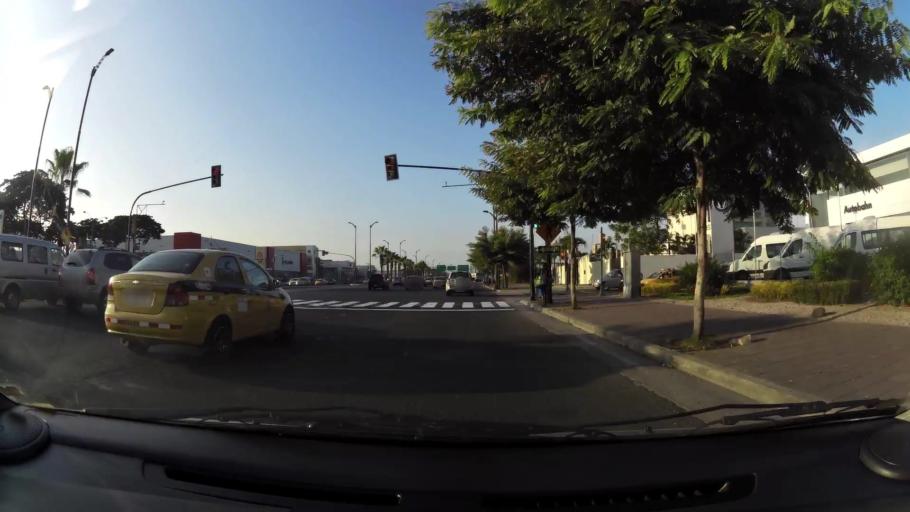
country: EC
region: Guayas
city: Eloy Alfaro
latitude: -2.1458
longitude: -79.8851
